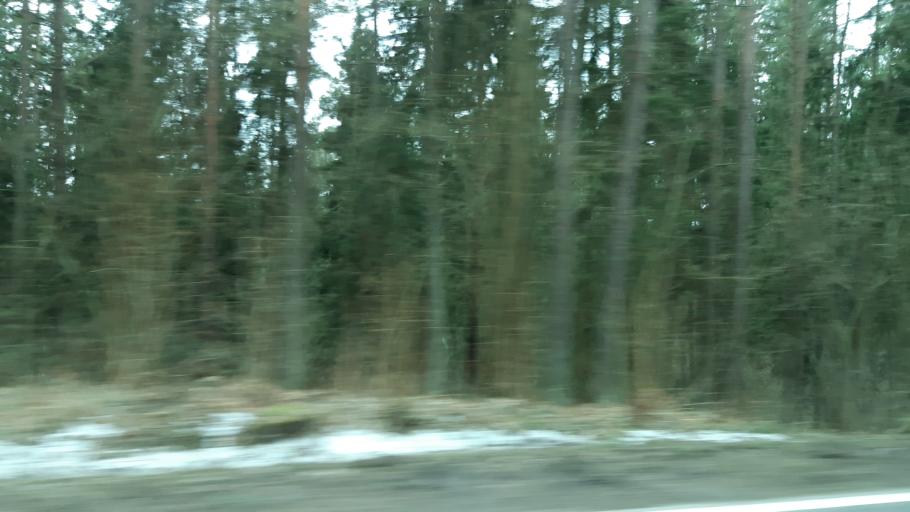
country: PL
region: Podlasie
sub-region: Suwalki
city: Suwalki
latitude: 54.3057
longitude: 22.9590
